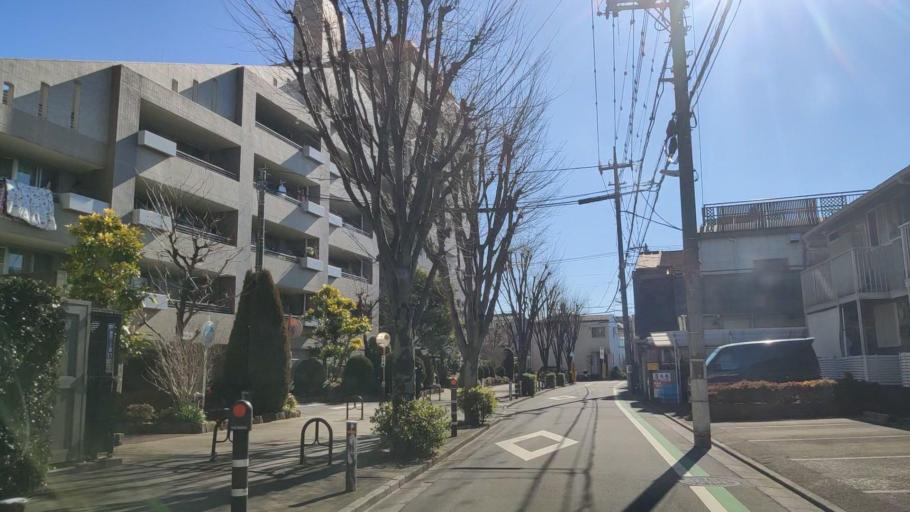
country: JP
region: Tokyo
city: Nishi-Tokyo-shi
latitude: 35.7236
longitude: 139.5518
